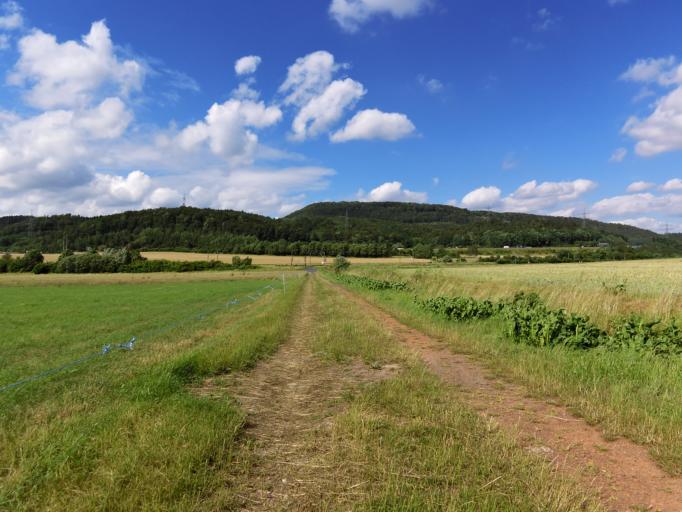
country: DE
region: Hesse
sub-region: Regierungsbezirk Kassel
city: Herleshausen
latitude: 51.0002
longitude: 10.1870
